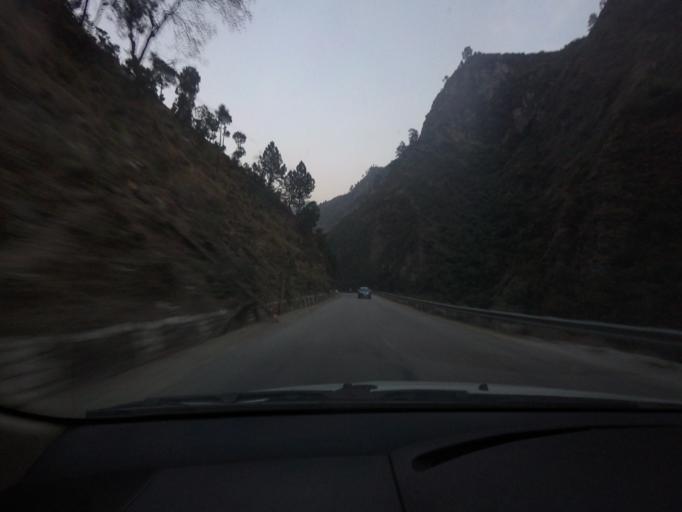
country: IN
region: Himachal Pradesh
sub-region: Mandi
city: Pandoh
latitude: 31.6948
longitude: 77.1453
